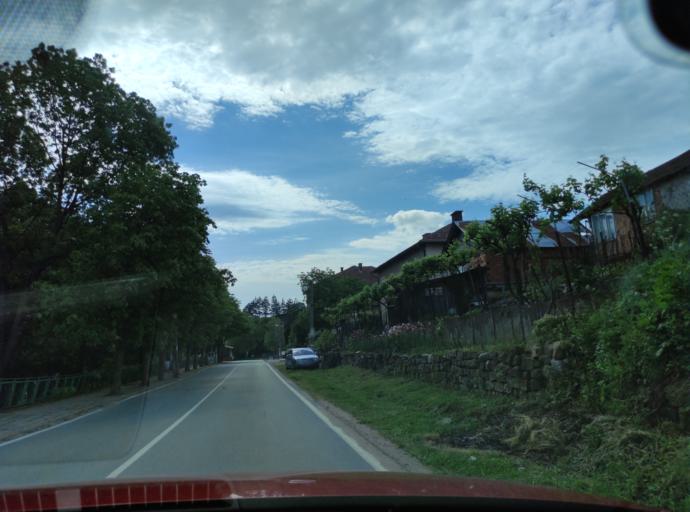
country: BG
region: Montana
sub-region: Obshtina Chiprovtsi
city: Chiprovtsi
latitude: 43.4690
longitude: 22.8607
